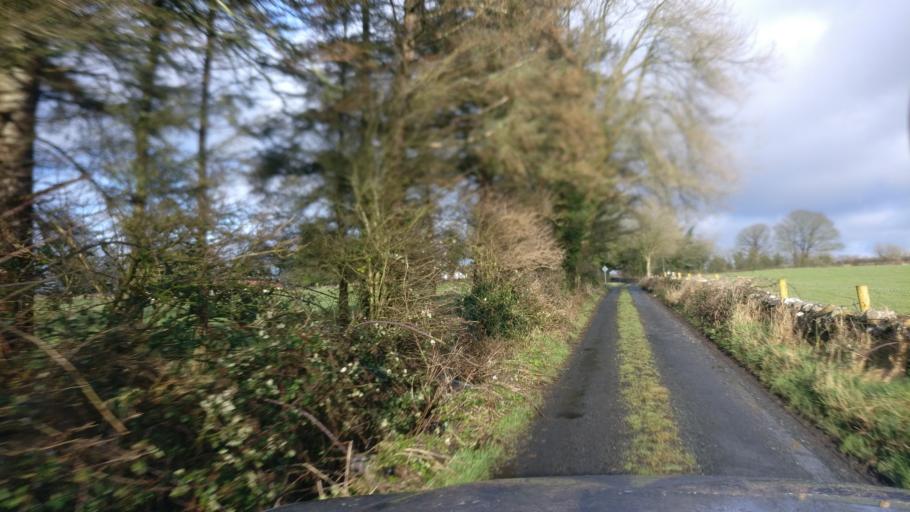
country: IE
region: Connaught
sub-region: County Galway
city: Loughrea
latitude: 53.2412
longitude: -8.5323
